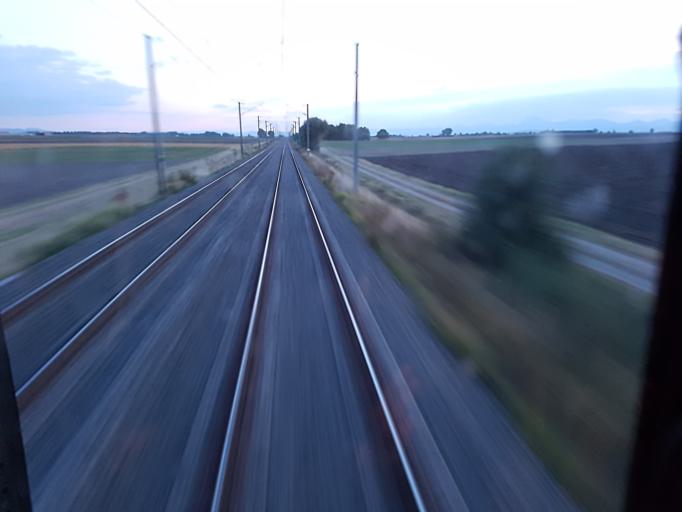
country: FR
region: Auvergne
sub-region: Departement du Puy-de-Dome
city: Ennezat
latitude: 45.9486
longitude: 3.2451
